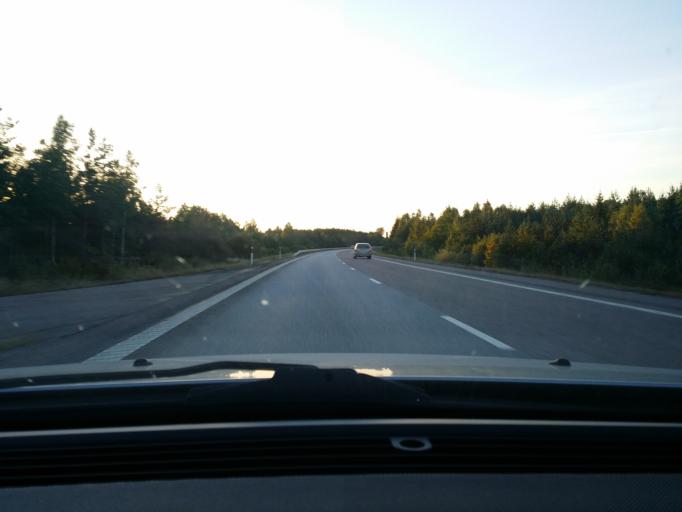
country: SE
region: Uppsala
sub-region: Enkopings Kommun
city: Dalby
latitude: 59.6134
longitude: 17.4094
